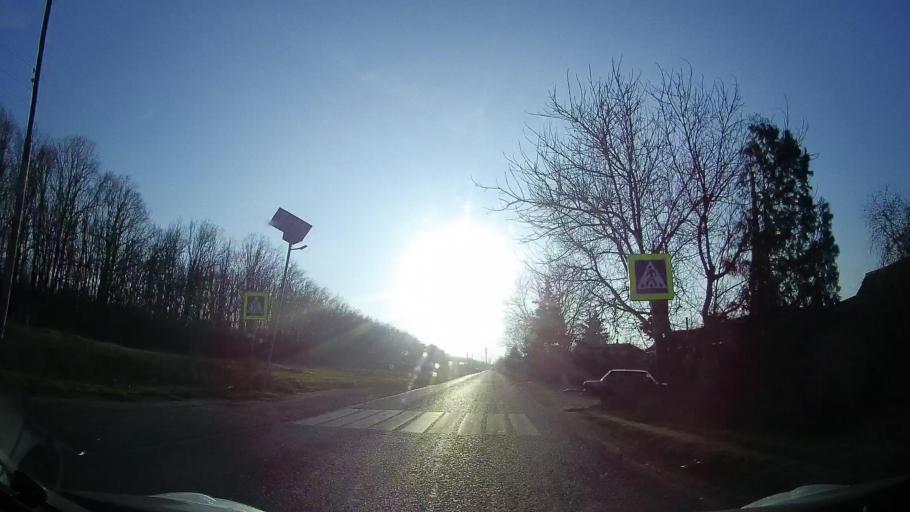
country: RU
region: Rostov
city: Ol'ginskaya
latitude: 47.1320
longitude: 39.8857
